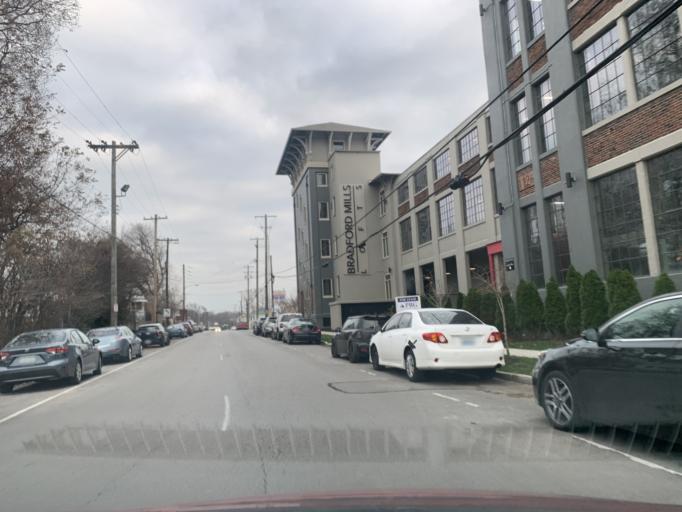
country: US
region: Kentucky
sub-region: Jefferson County
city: Audubon Park
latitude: 38.2328
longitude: -85.7358
